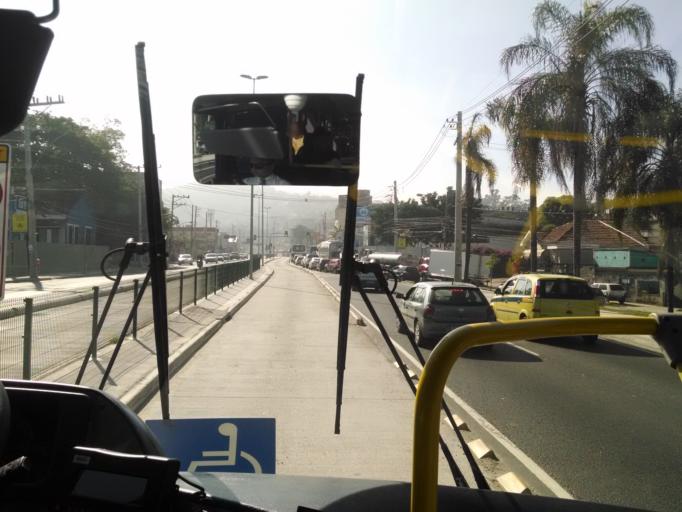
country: BR
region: Rio de Janeiro
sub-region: Sao Joao De Meriti
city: Sao Joao de Meriti
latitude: -22.9185
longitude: -43.3651
